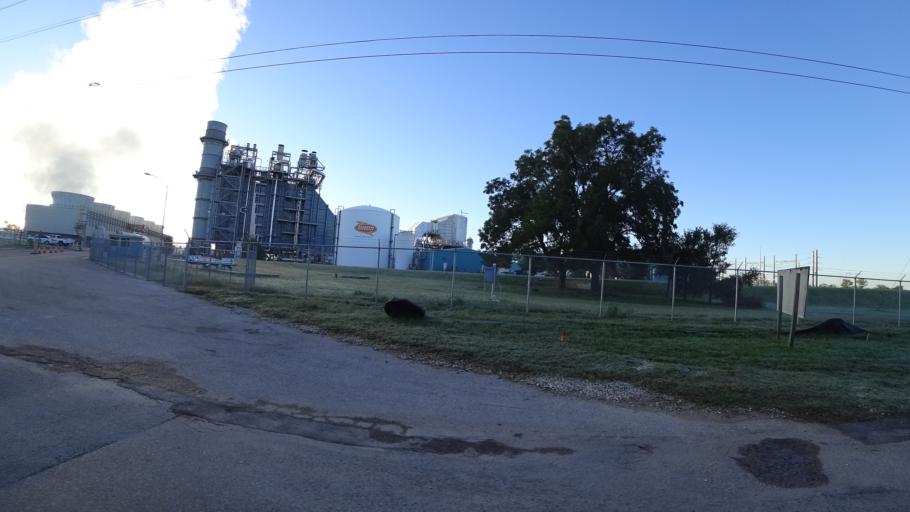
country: US
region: Texas
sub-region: Travis County
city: Hornsby Bend
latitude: 30.2116
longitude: -97.6136
